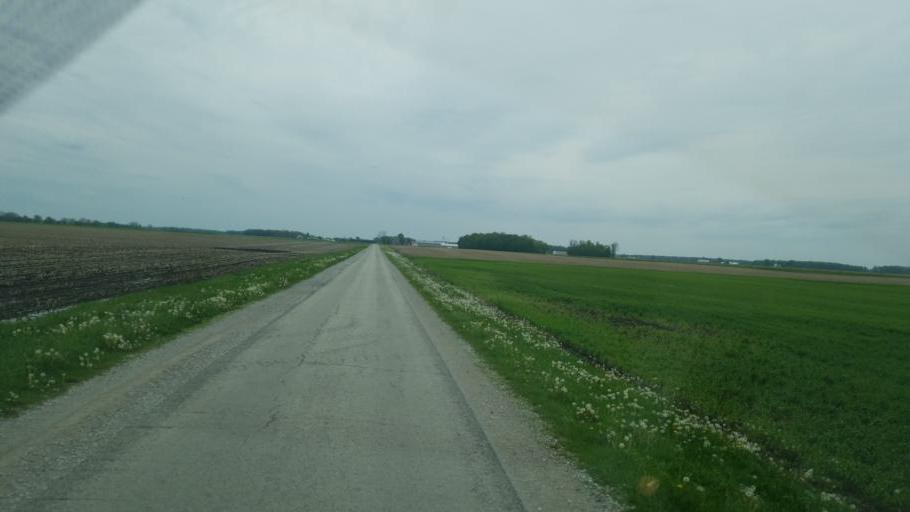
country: US
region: Ohio
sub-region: Huron County
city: Willard
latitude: 41.0290
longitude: -82.7993
